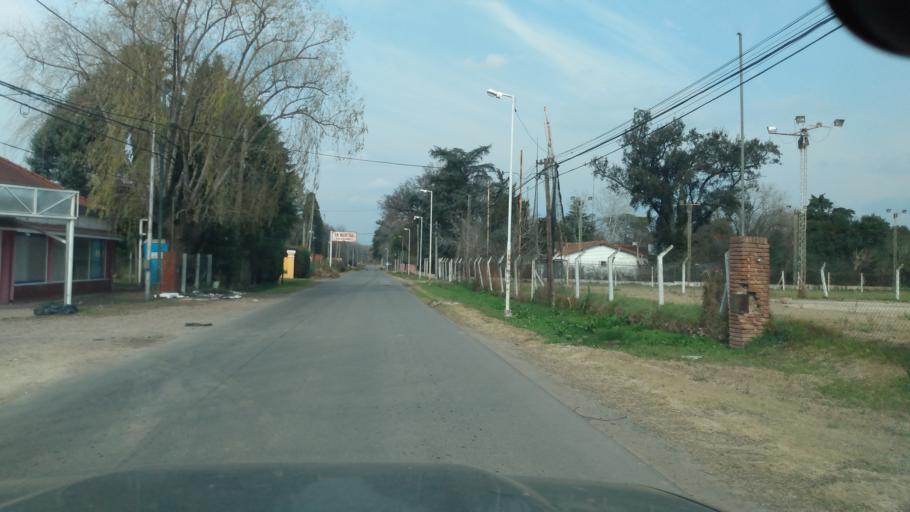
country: AR
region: Buenos Aires
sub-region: Partido de Lujan
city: Lujan
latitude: -34.5564
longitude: -59.1249
